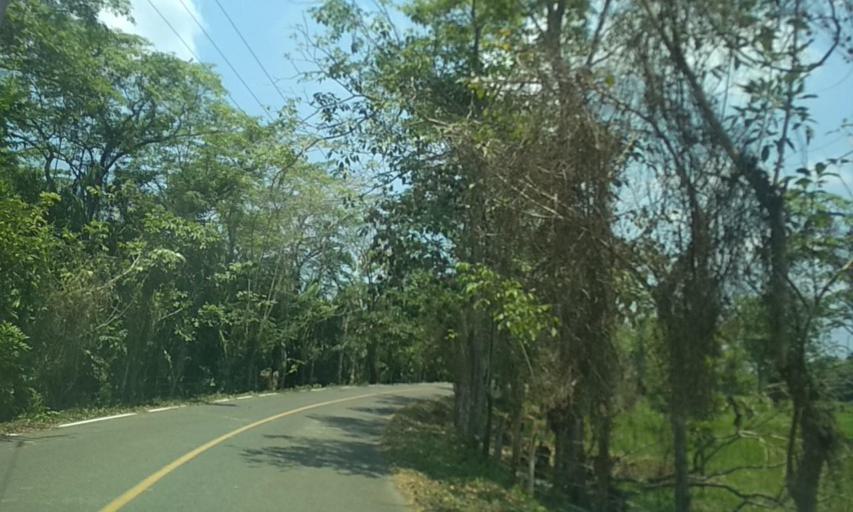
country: MX
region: Tabasco
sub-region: Huimanguillo
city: Francisco Rueda
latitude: 17.7539
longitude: -94.0297
